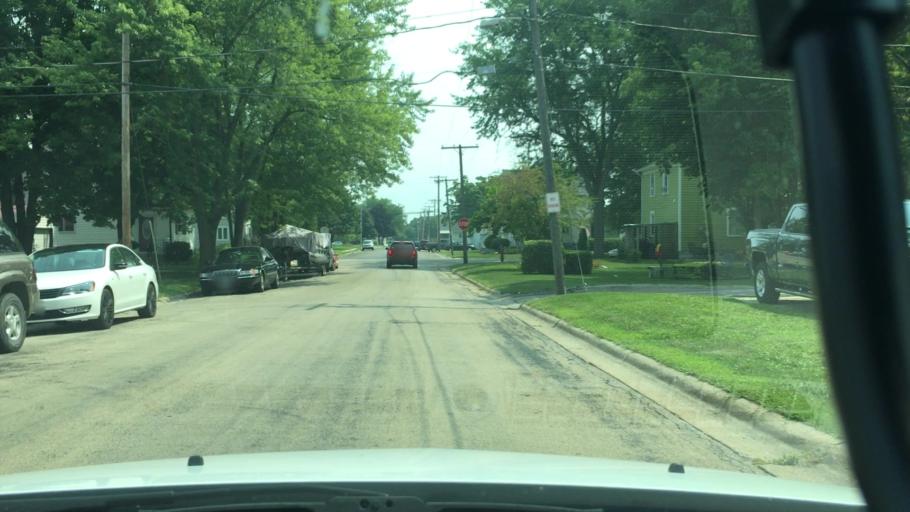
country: US
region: Illinois
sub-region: Ogle County
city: Rochelle
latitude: 41.9270
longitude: -89.0661
